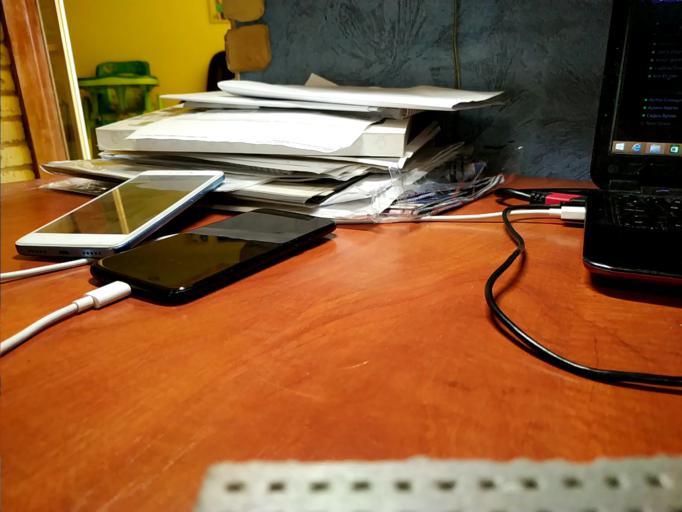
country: RU
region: Tverskaya
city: Spirovo
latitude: 57.4200
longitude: 35.1110
